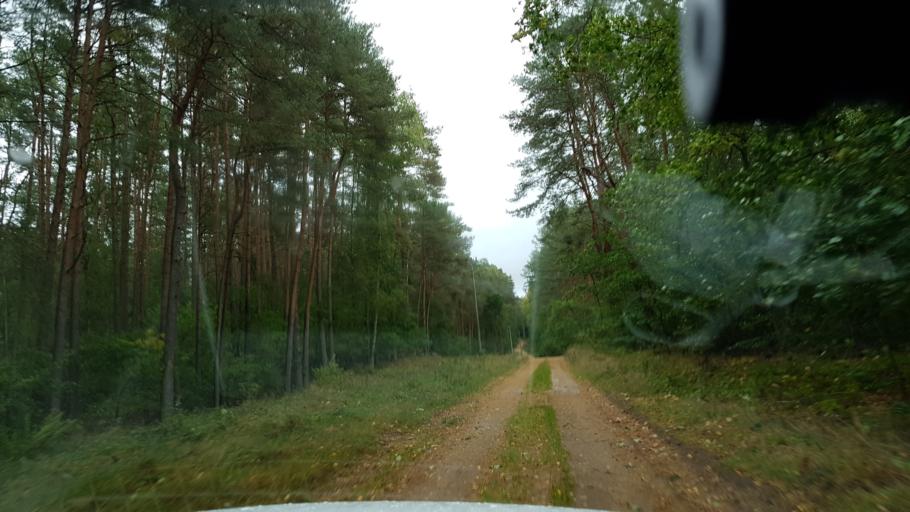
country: PL
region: West Pomeranian Voivodeship
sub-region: Powiat goleniowski
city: Przybiernow
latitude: 53.7499
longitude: 14.7509
